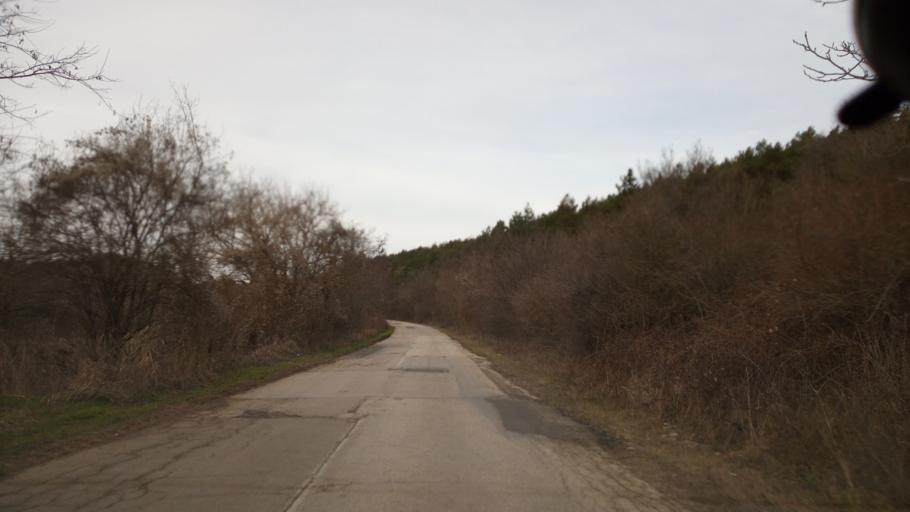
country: BG
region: Pleven
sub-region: Obshtina Nikopol
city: Nikopol
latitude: 43.5964
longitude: 24.9871
